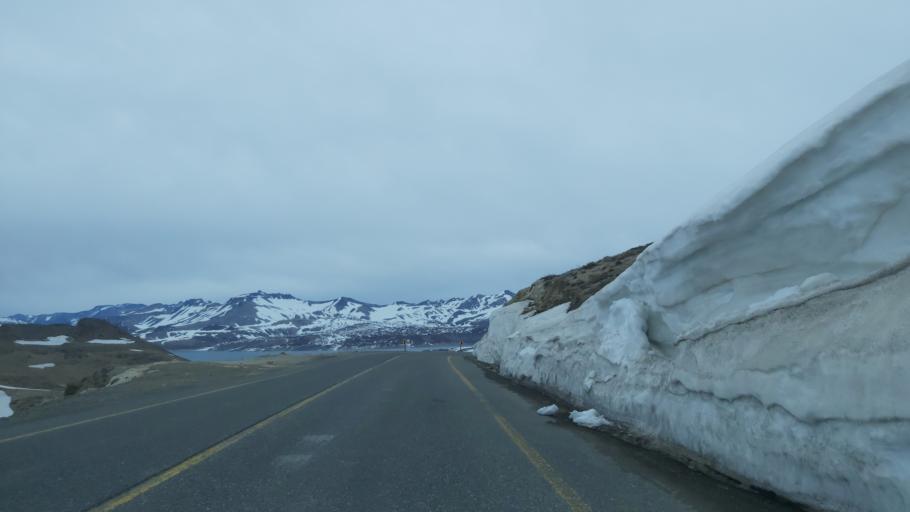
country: CL
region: Maule
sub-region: Provincia de Linares
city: Colbun
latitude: -36.0195
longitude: -70.4990
